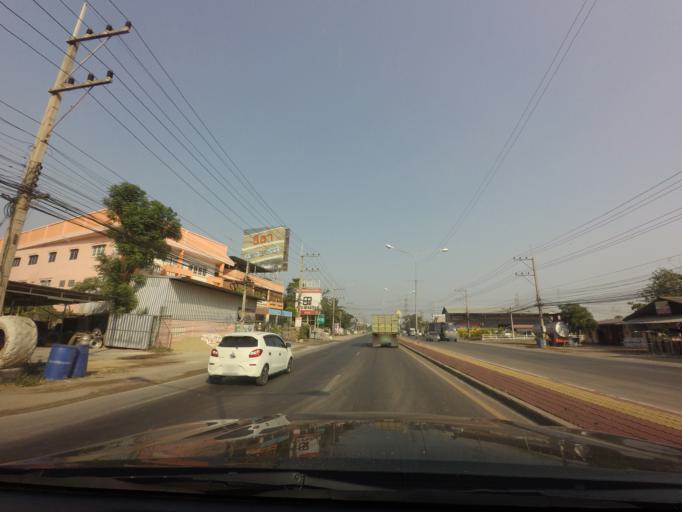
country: TH
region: Ratchaburi
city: Ban Pong
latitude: 13.8481
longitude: 99.8545
